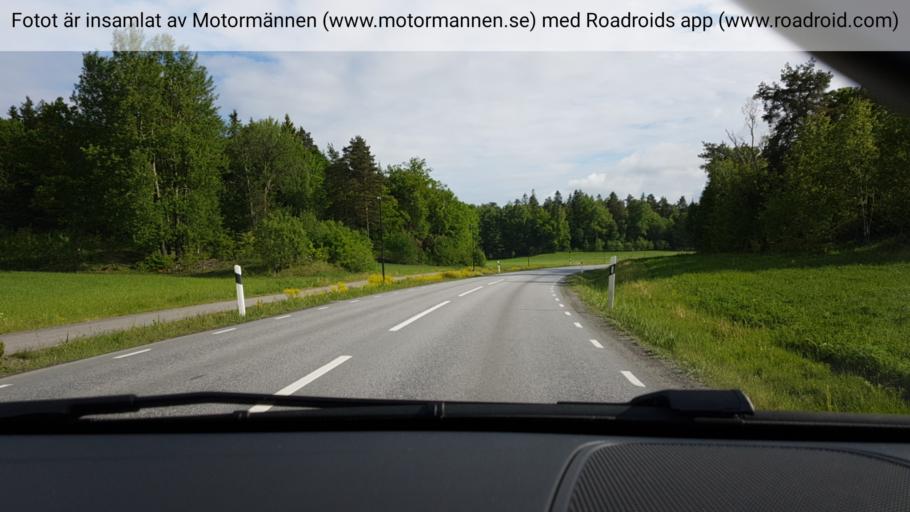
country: SE
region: Stockholm
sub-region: Huddinge Kommun
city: Huddinge
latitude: 59.2125
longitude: 18.0146
